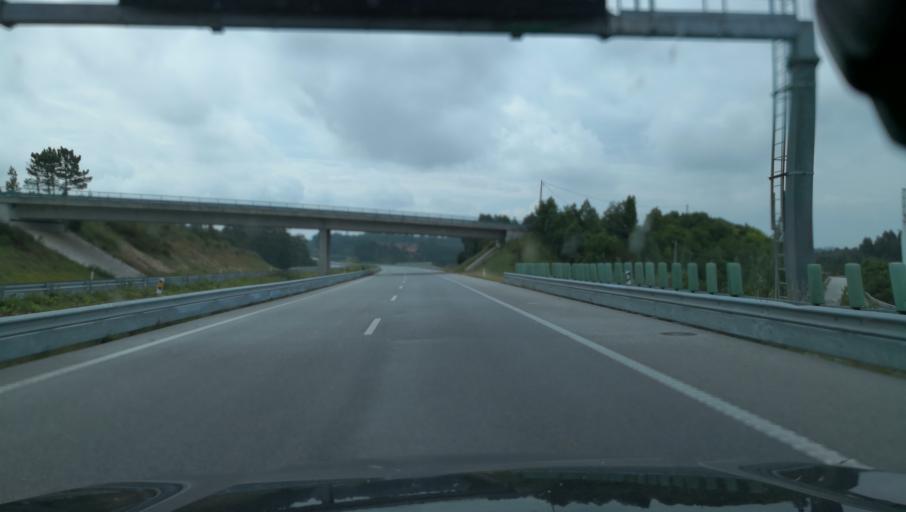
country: PT
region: Coimbra
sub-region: Figueira da Foz
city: Alhadas
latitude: 40.1814
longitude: -8.8061
